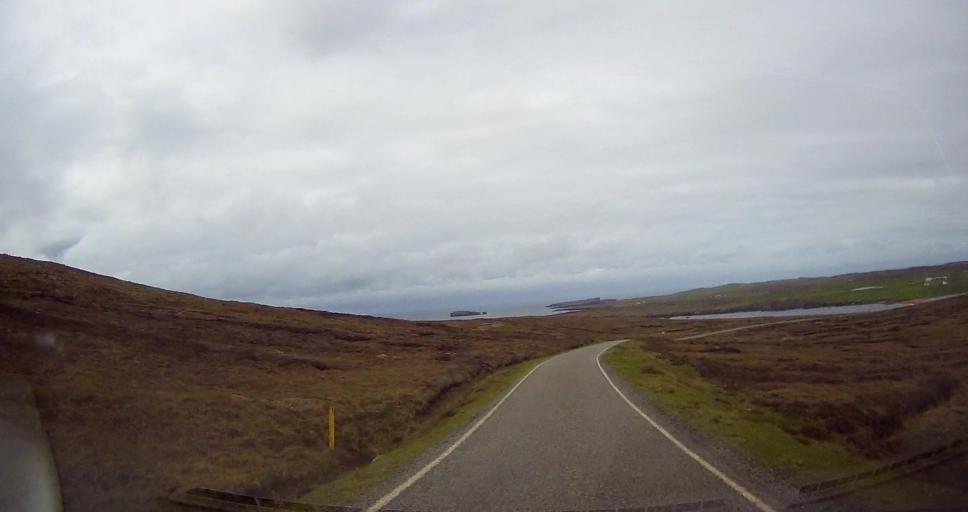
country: GB
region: Scotland
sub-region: Shetland Islands
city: Lerwick
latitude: 60.4875
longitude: -1.5307
